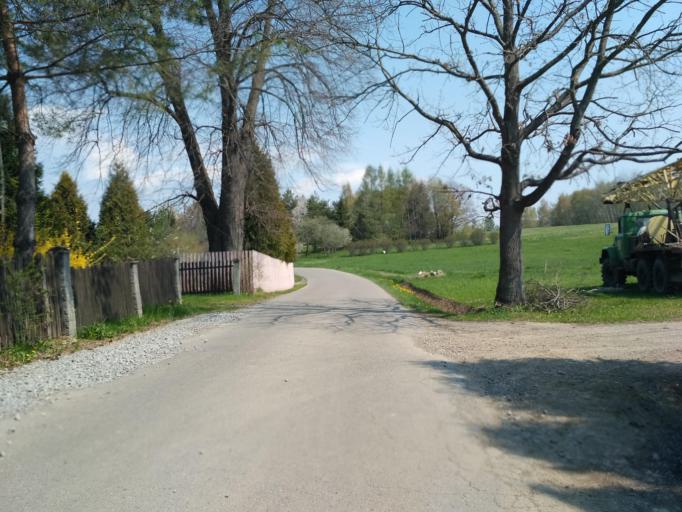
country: PL
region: Subcarpathian Voivodeship
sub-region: Powiat krosnienski
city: Chorkowka
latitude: 49.6243
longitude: 21.7031
